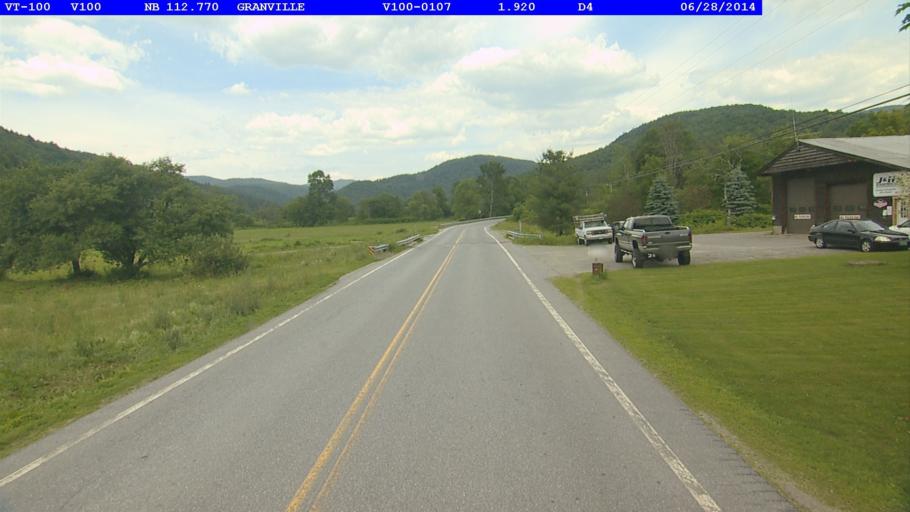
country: US
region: Vermont
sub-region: Orange County
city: Randolph
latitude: 43.9718
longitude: -72.8433
